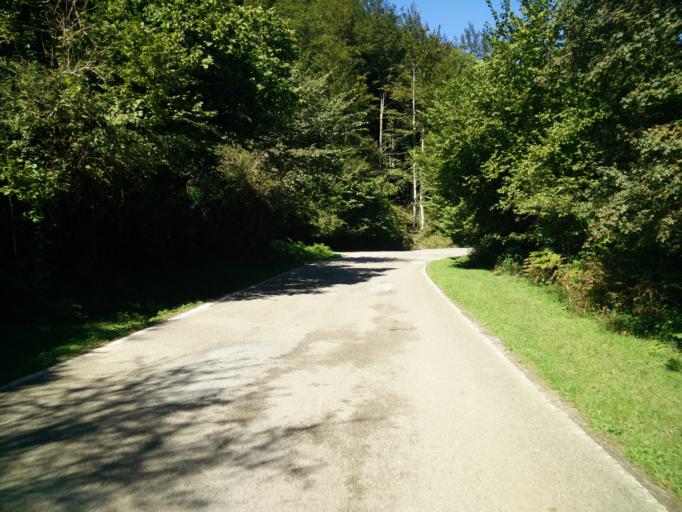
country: ES
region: Cantabria
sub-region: Provincia de Cantabria
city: Ruente
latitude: 43.1246
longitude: -4.2968
